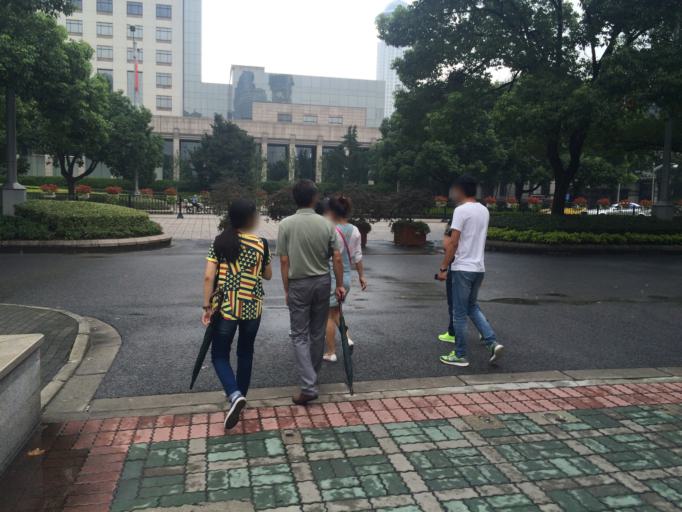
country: CN
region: Shanghai Shi
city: Shanghai
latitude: 31.2319
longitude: 121.4703
